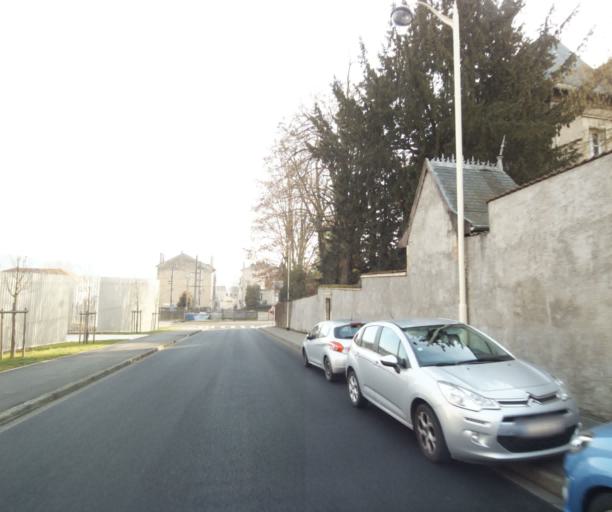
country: FR
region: Lorraine
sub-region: Departement de Meurthe-et-Moselle
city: Maxeville
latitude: 48.7032
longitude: 6.1667
